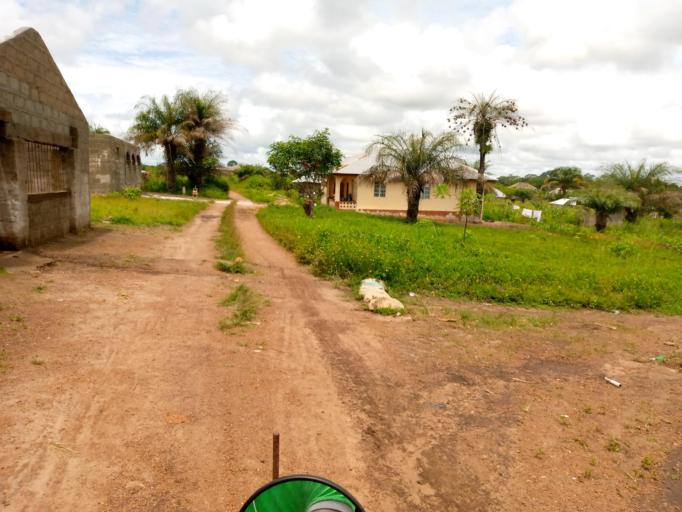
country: SL
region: Northern Province
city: Magburaka
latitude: 8.7209
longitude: -11.9244
